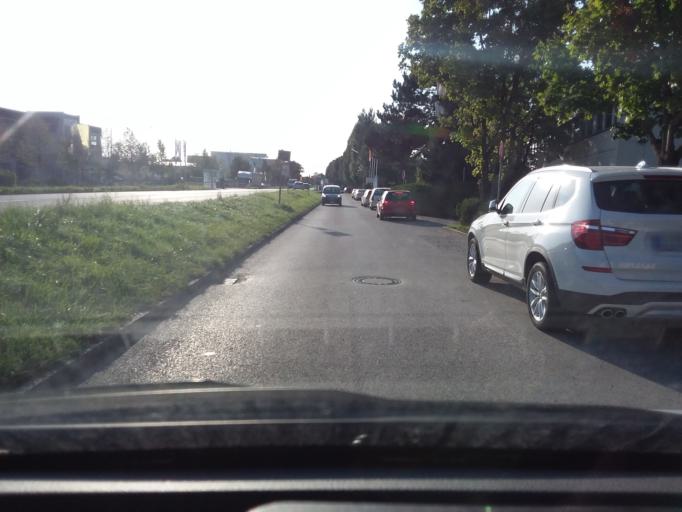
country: DE
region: Bavaria
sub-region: Upper Bavaria
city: Garching bei Munchen
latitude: 48.2499
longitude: 11.6237
